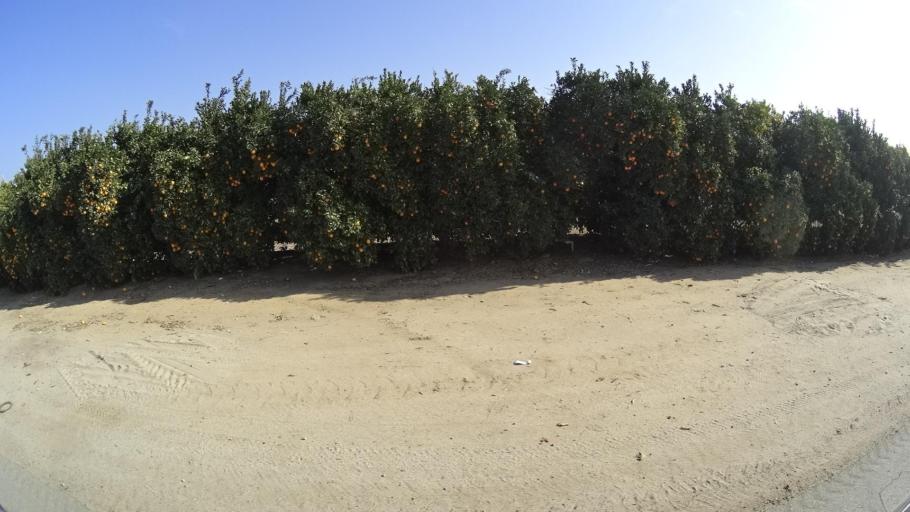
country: US
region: California
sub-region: Kern County
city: McFarland
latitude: 35.6097
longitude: -119.1865
